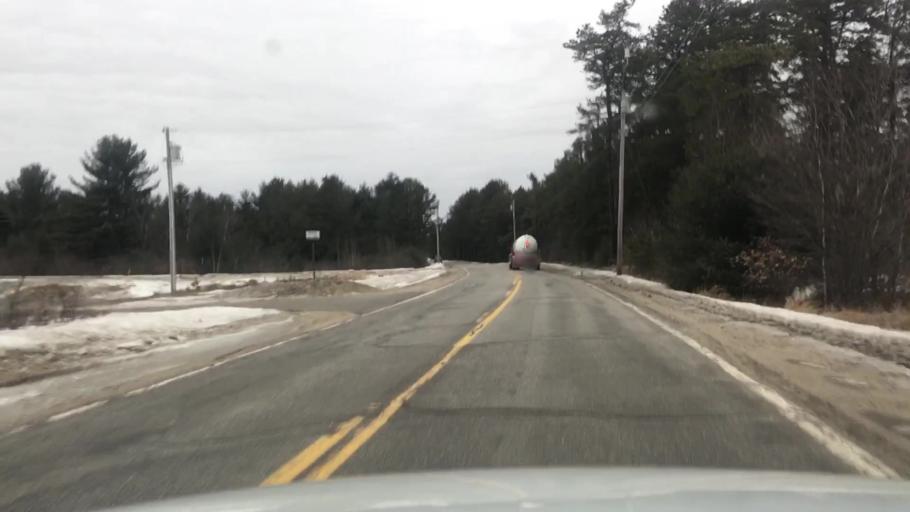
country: US
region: Maine
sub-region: York County
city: Shapleigh
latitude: 43.5672
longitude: -70.8592
